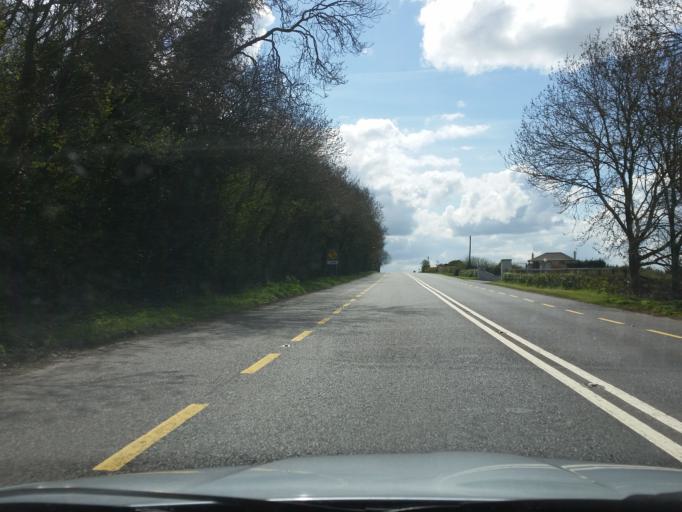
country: IE
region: Leinster
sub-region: An Mhi
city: Slane
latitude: 53.6894
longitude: -6.5413
